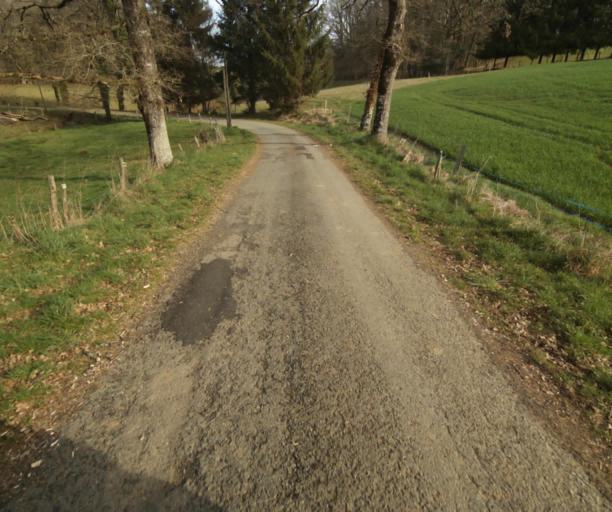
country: FR
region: Limousin
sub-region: Departement de la Correze
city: Chamboulive
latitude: 45.4276
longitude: 1.7593
